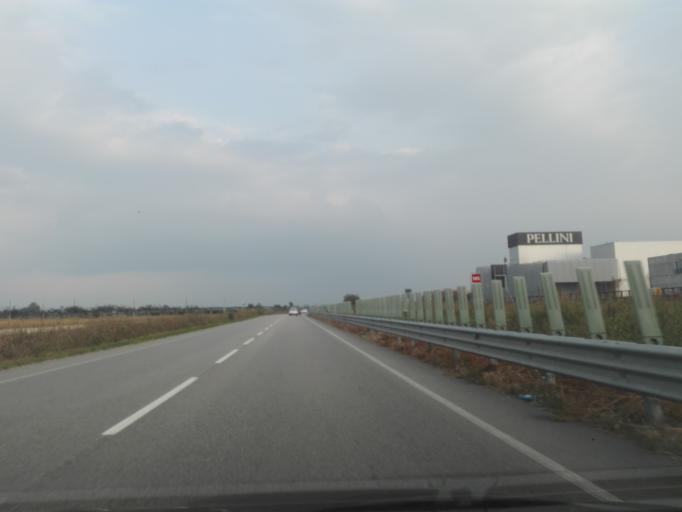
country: IT
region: Veneto
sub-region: Provincia di Verona
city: Bussolengo
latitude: 45.4538
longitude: 10.8649
